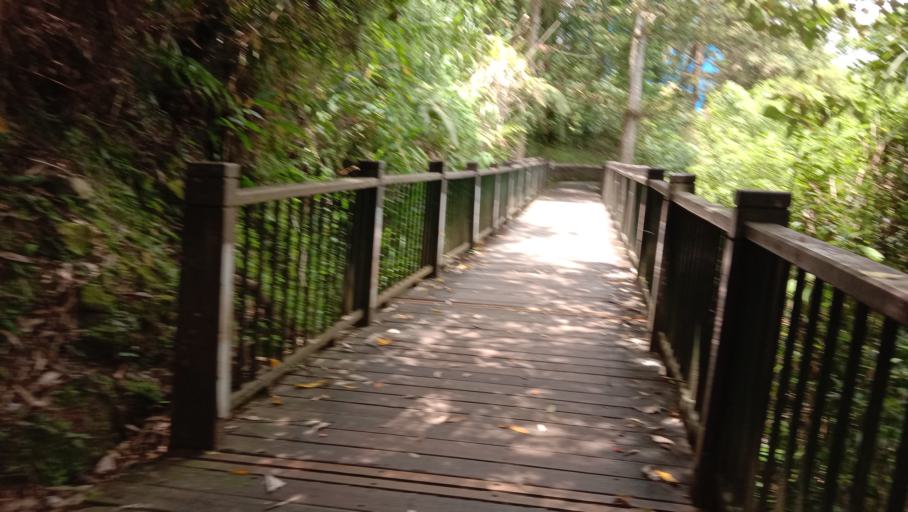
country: TW
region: Taiwan
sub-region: Nantou
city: Puli
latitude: 23.8496
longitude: 120.9331
